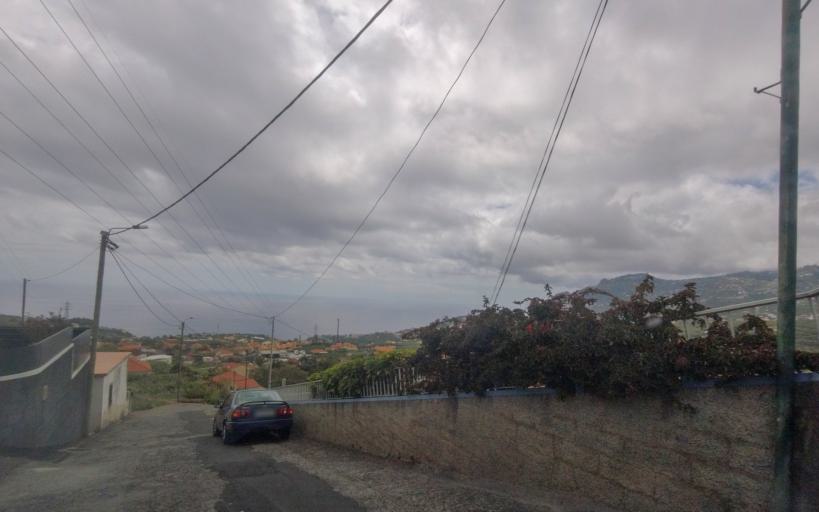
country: PT
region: Madeira
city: Camara de Lobos
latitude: 32.6587
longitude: -16.9524
